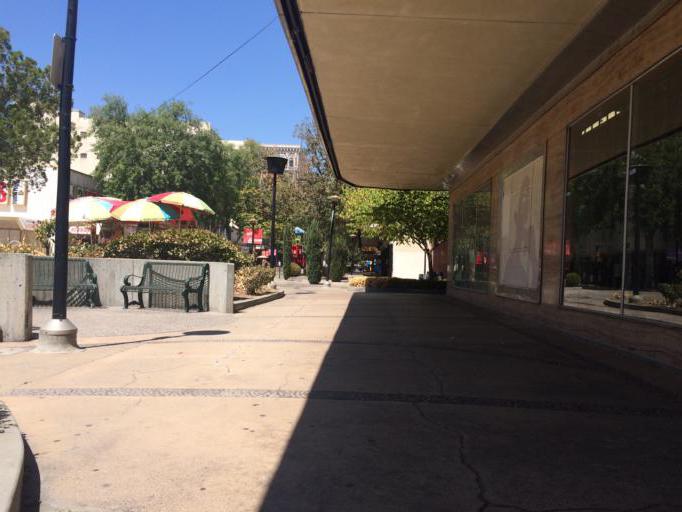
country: US
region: California
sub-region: Fresno County
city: Fresno
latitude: 36.7327
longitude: -119.7888
